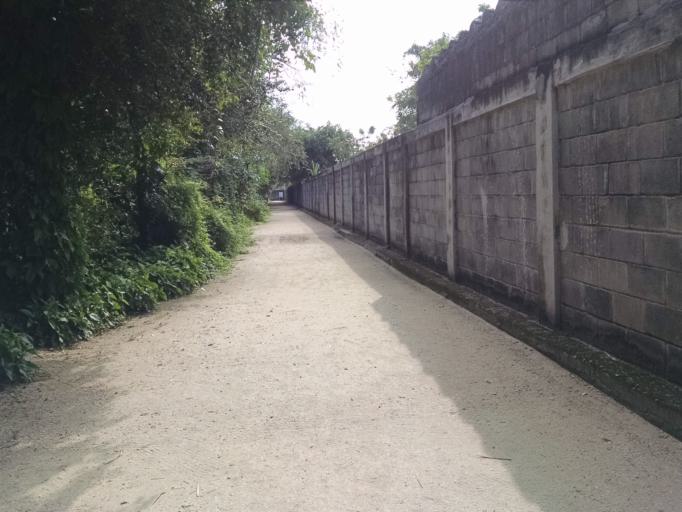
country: BR
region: Rio de Janeiro
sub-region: Rio De Janeiro
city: Rio de Janeiro
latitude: -22.9949
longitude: -43.3693
